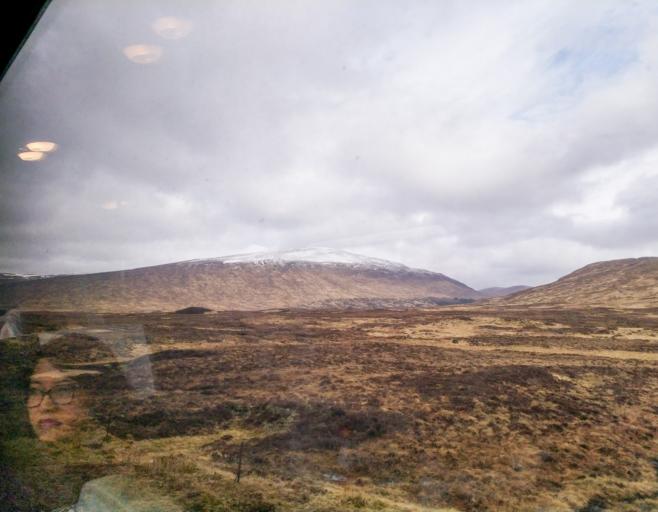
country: GB
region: Scotland
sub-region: Highland
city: Spean Bridge
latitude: 56.7481
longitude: -4.6738
